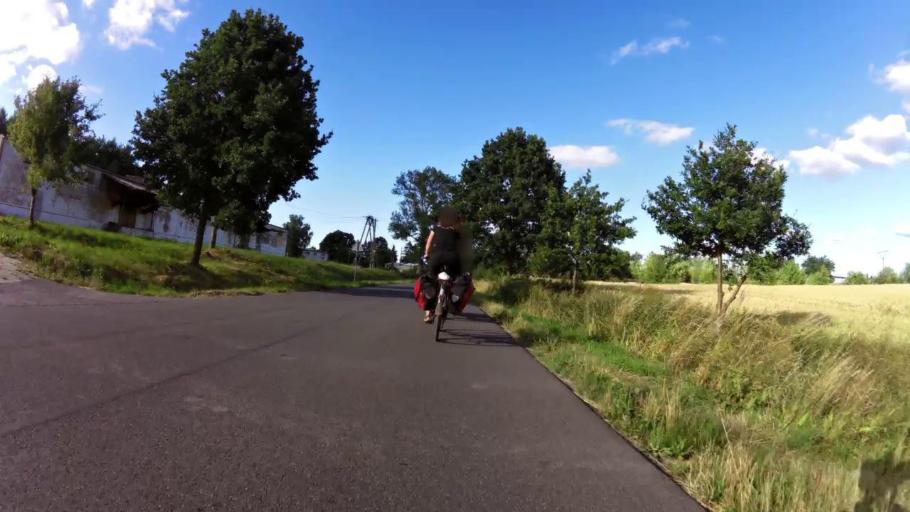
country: PL
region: West Pomeranian Voivodeship
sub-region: Powiat swidwinski
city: Swidwin
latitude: 53.6948
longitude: 15.7823
